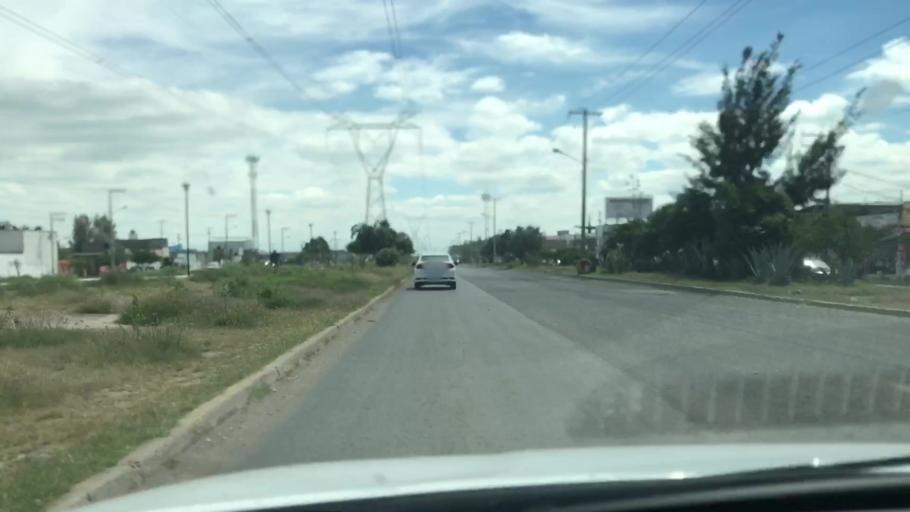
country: MX
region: Guanajuato
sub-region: Celaya
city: La Trinidad
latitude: 20.5489
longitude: -100.7872
